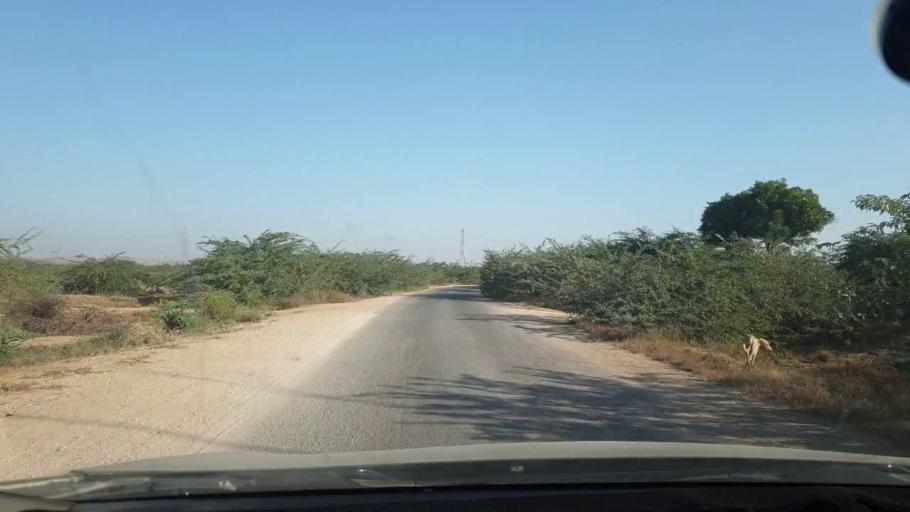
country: PK
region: Sindh
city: Malir Cantonment
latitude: 25.1550
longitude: 67.1911
